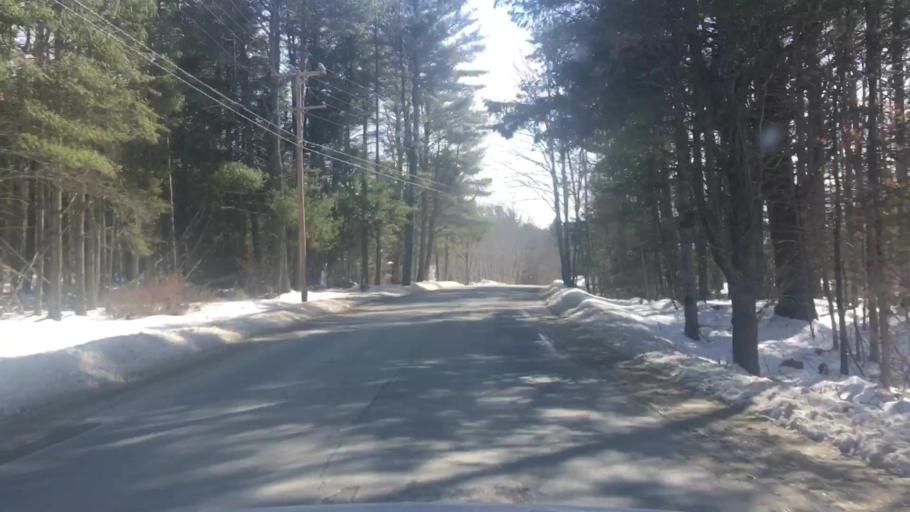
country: US
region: Maine
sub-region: Penobscot County
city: Holden
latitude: 44.7532
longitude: -68.6343
